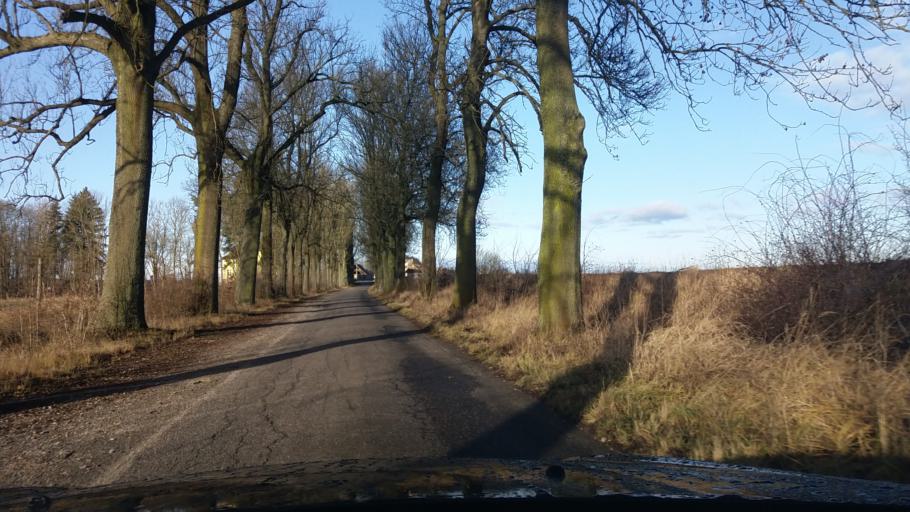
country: PL
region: West Pomeranian Voivodeship
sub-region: Powiat choszczenski
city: Drawno
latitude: 53.1908
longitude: 15.7911
